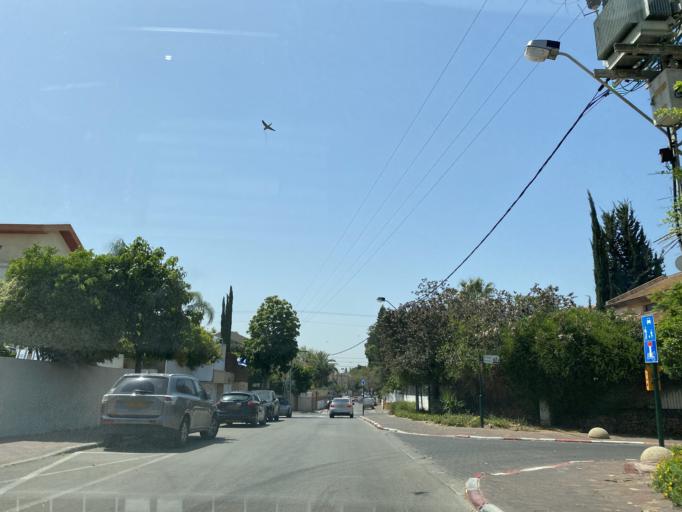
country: IL
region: Central District
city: Ra'anana
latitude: 32.1892
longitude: 34.8706
